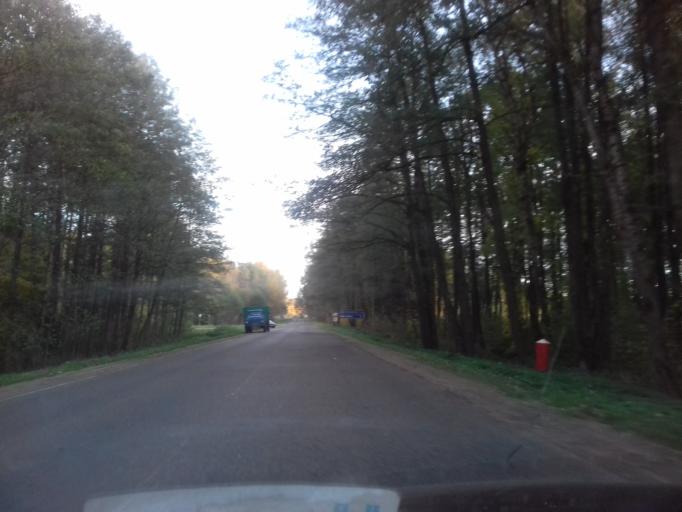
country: BY
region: Minsk
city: Hatava
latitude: 53.7552
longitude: 27.6600
